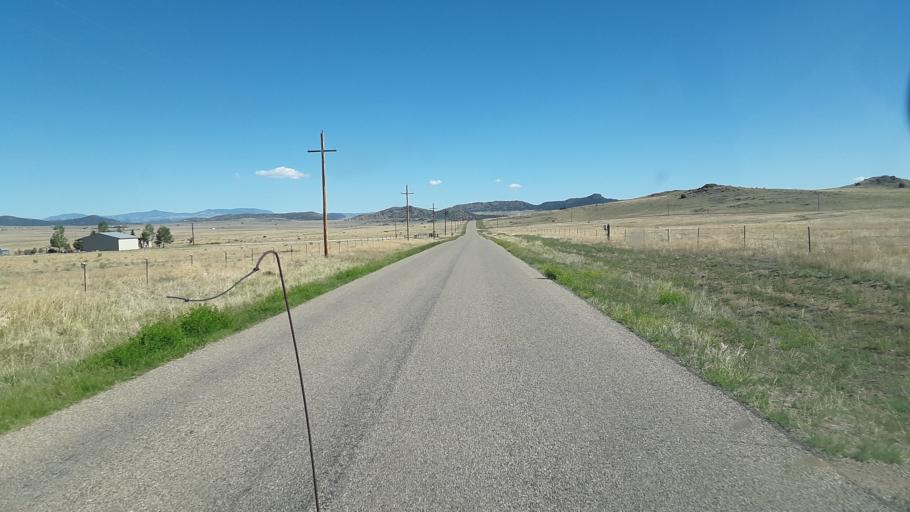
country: US
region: Colorado
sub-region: Custer County
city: Westcliffe
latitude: 38.1729
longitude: -105.4617
